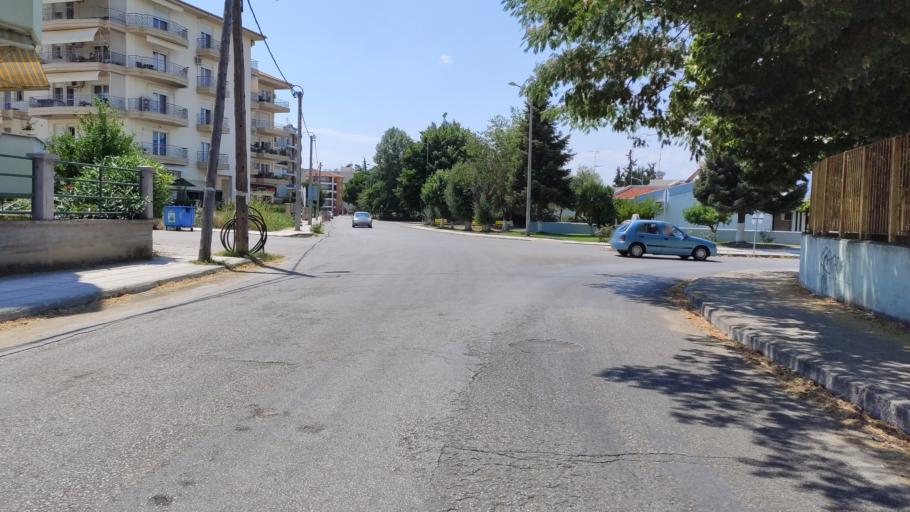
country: GR
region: East Macedonia and Thrace
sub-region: Nomos Rodopis
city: Komotini
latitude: 41.1210
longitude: 25.3930
